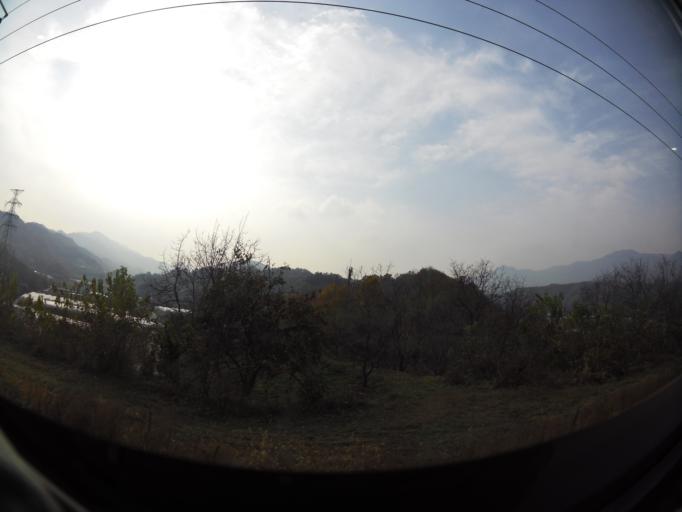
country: KR
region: Gyeongsangbuk-do
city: Gimcheon
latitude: 36.1279
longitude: 128.0275
